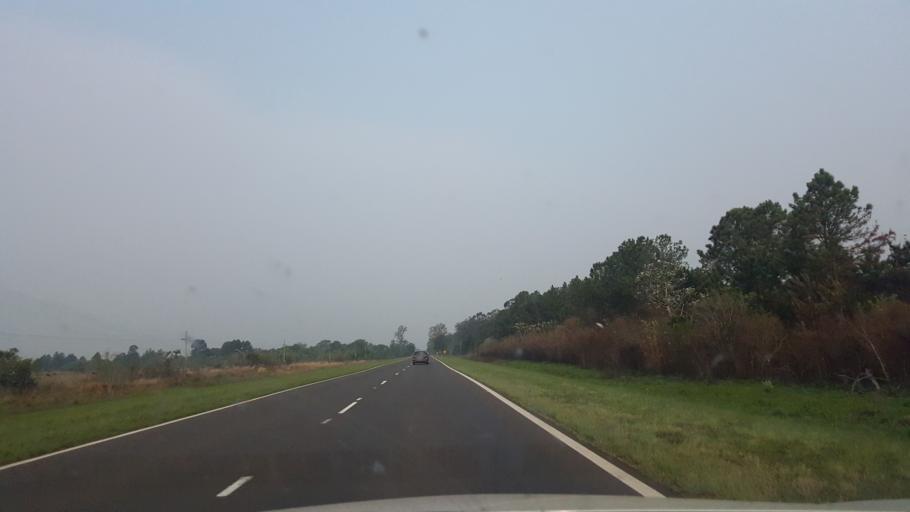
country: AR
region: Corrientes
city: Ita Ibate
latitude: -27.5094
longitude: -57.2395
